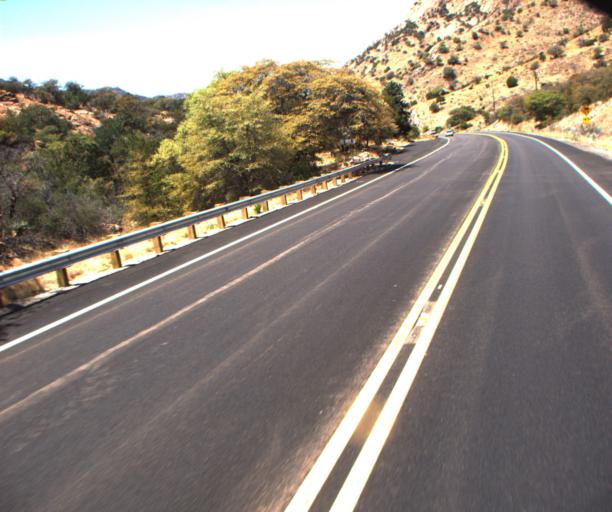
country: US
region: Arizona
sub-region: Cochise County
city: Bisbee
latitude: 31.4639
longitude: -109.9496
